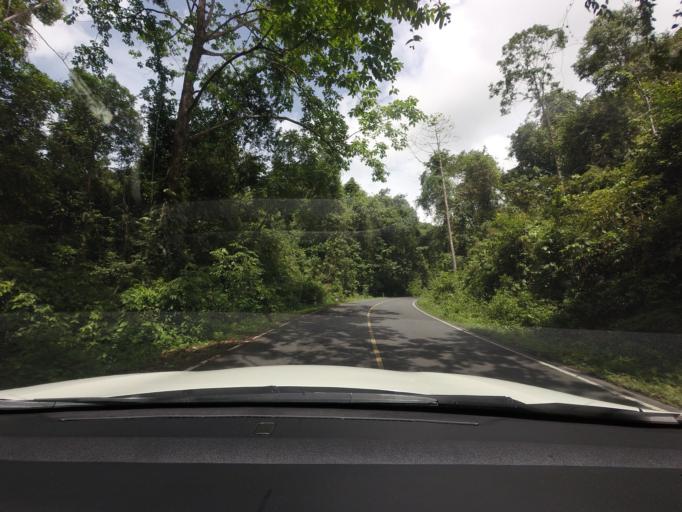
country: TH
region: Nakhon Nayok
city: Pak Phli
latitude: 14.3212
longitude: 101.3699
